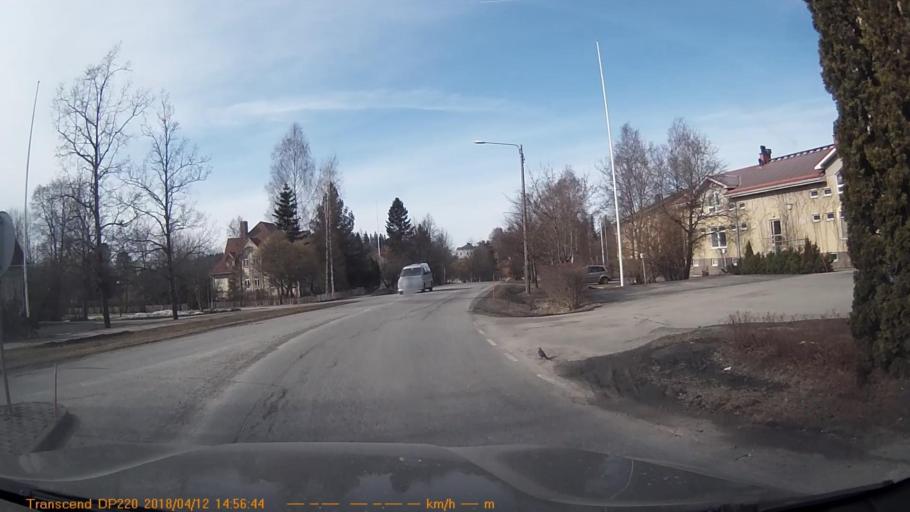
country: FI
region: Haeme
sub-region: Forssa
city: Jokioinen
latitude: 60.8116
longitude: 23.4824
